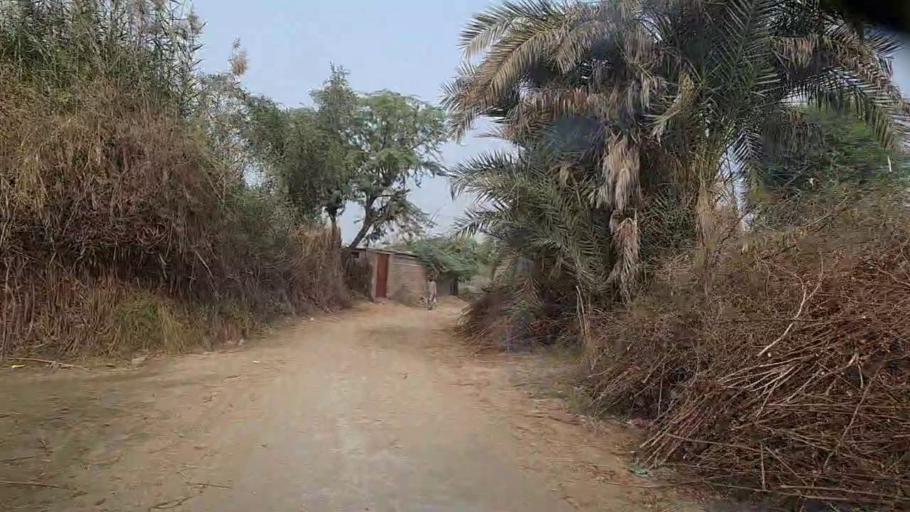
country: PK
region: Sindh
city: Bozdar
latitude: 27.1453
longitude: 68.6508
